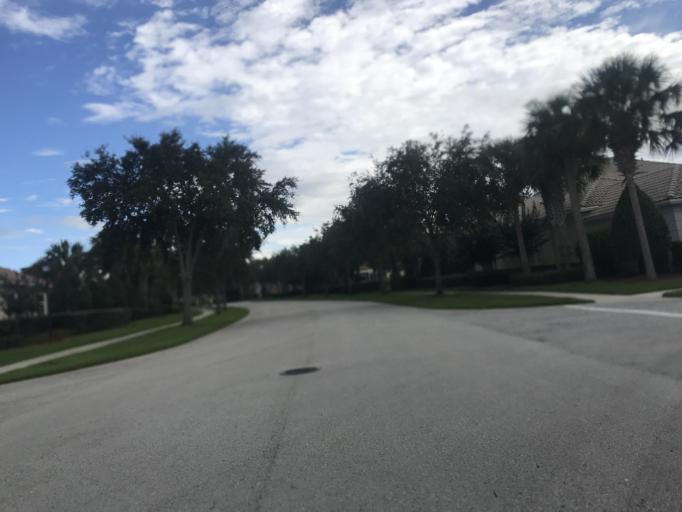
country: US
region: Florida
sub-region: Indian River County
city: Gifford
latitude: 27.6881
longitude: -80.4425
